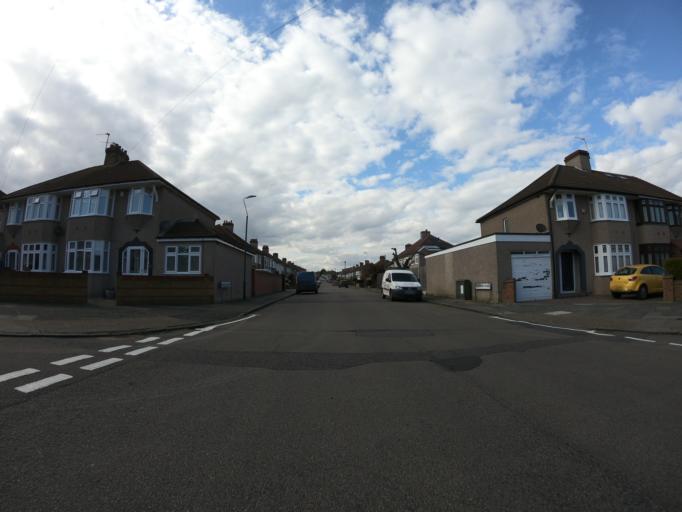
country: GB
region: England
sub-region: Greater London
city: Bexleyheath
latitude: 51.4746
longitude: 0.1374
